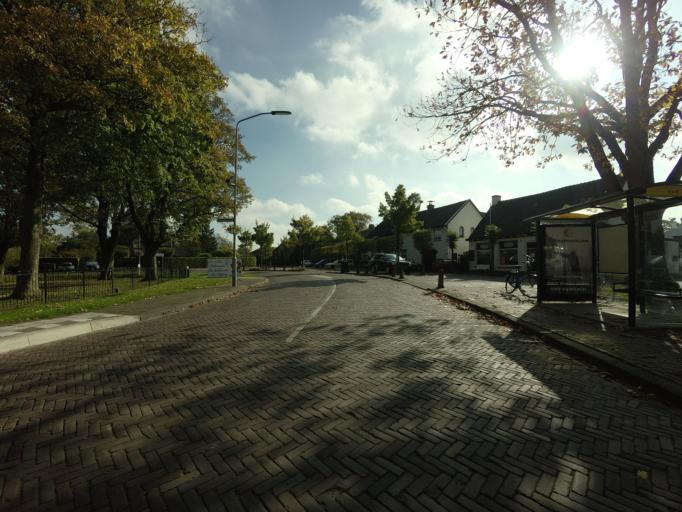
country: NL
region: Utrecht
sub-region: Gemeente Wijk bij Duurstede
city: Wijk bij Duurstede
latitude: 51.9424
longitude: 5.3106
